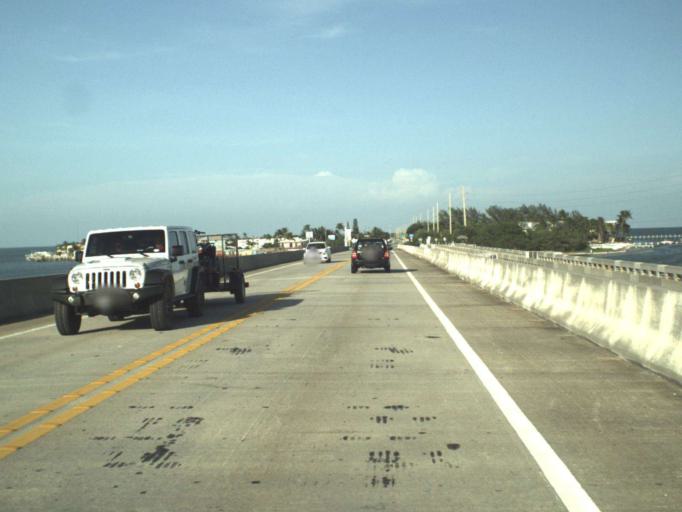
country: US
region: Florida
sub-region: Monroe County
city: Marathon
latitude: 24.8024
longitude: -80.8527
